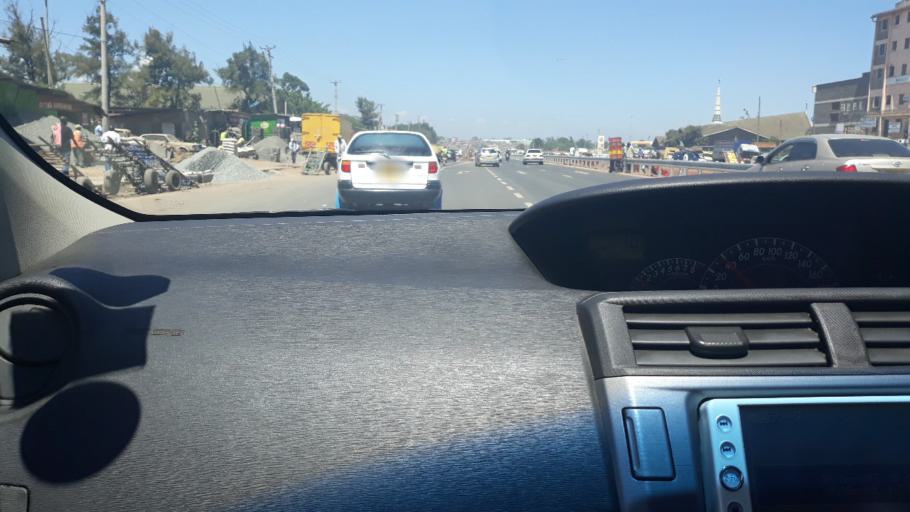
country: KE
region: Nairobi Area
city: Pumwani
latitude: -1.2586
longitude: 36.8788
